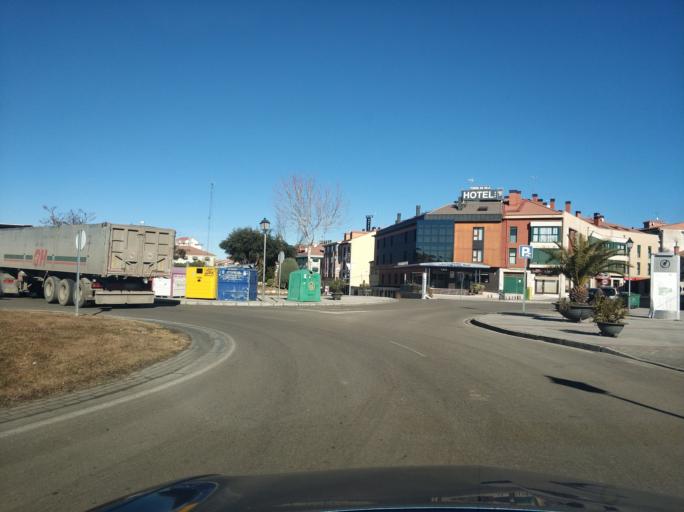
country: ES
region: Castille and Leon
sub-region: Provincia de Valladolid
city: Tordesillas
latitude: 41.5017
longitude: -5.0043
